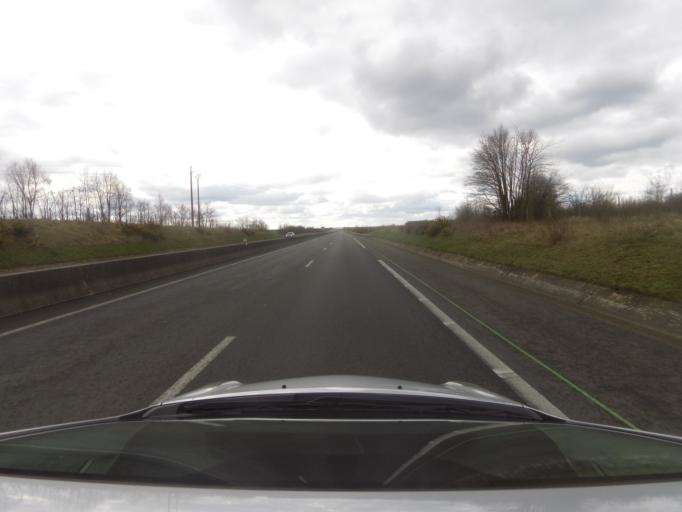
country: FR
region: Nord-Pas-de-Calais
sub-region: Departement du Pas-de-Calais
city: Saint-Josse
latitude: 50.4393
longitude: 1.6929
